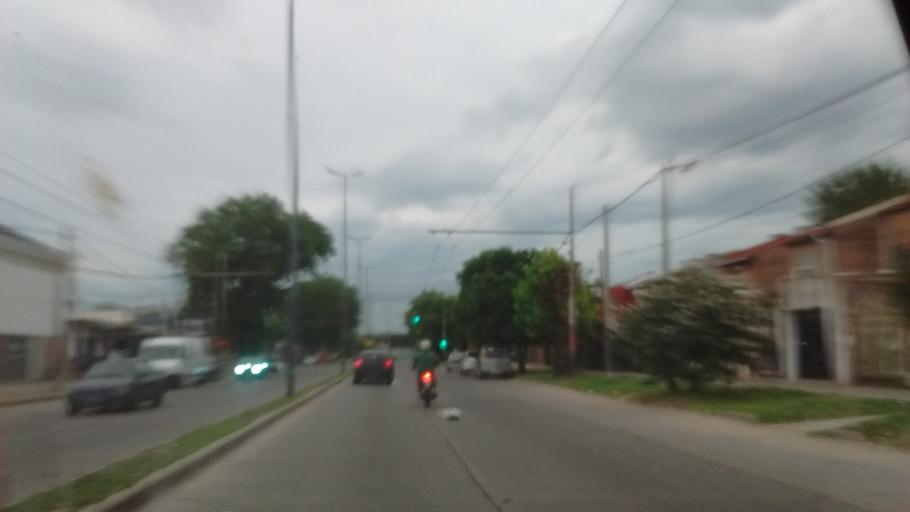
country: AR
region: Santa Fe
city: Perez
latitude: -32.9406
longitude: -60.7284
